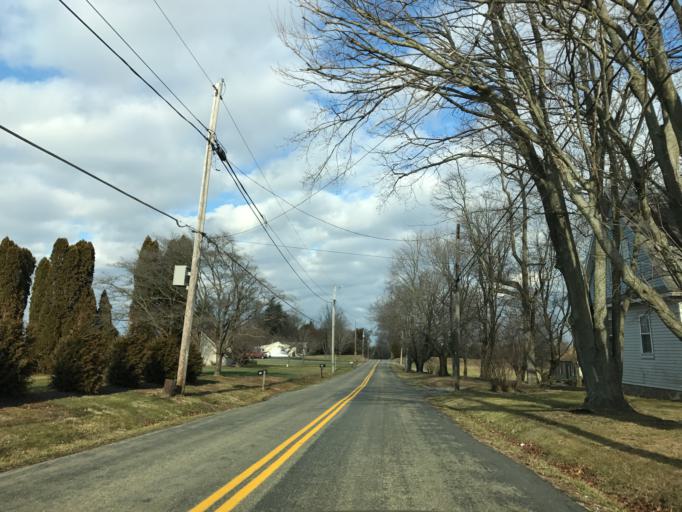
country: US
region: Maryland
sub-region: Harford County
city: Aberdeen
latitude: 39.6403
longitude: -76.1895
